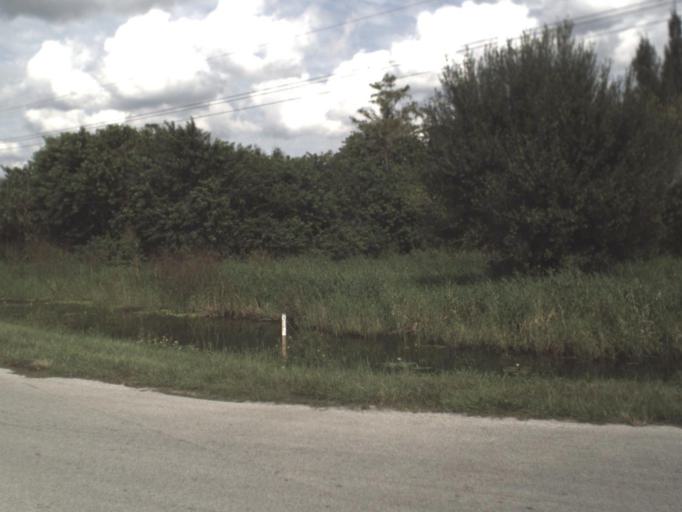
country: US
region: Florida
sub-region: Hendry County
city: Port LaBelle
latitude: 26.6645
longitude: -81.4363
